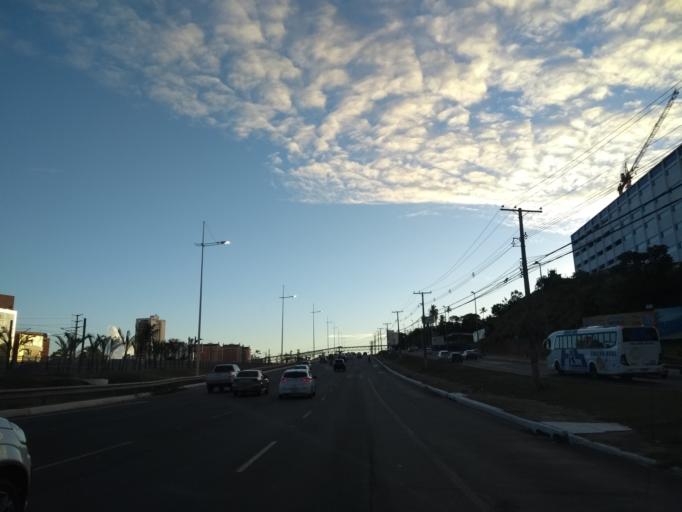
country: BR
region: Bahia
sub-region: Salvador
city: Salvador
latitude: -12.9587
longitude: -38.4318
